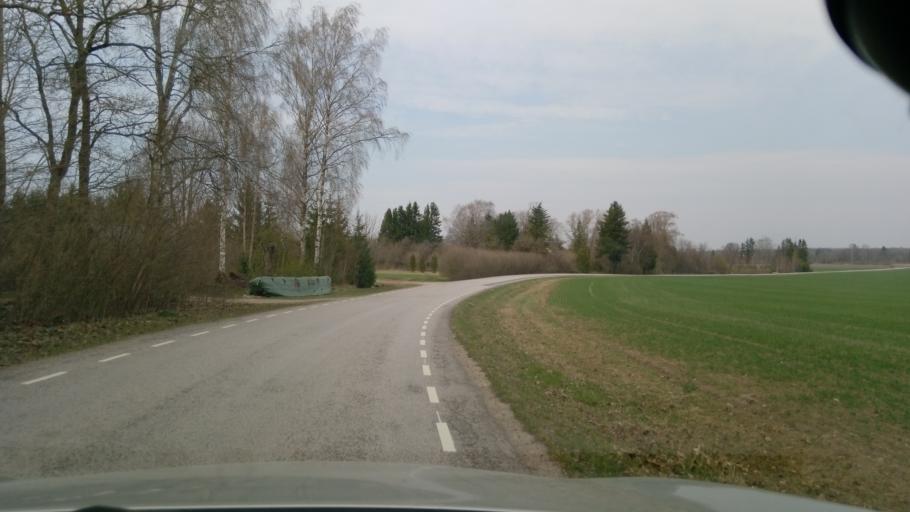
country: EE
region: Jaervamaa
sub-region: Tueri vald
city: Sarevere
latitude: 58.7854
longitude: 25.4741
